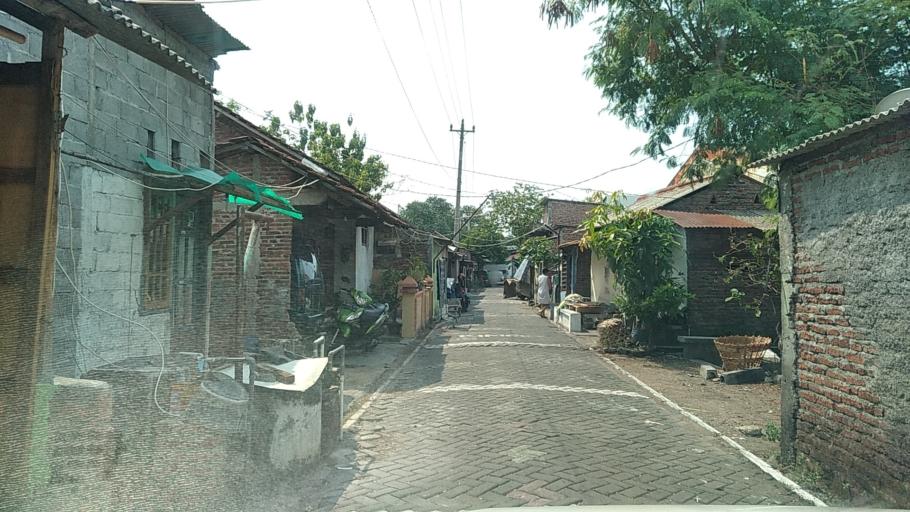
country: ID
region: Central Java
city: Semarang
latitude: -6.9997
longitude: 110.4404
